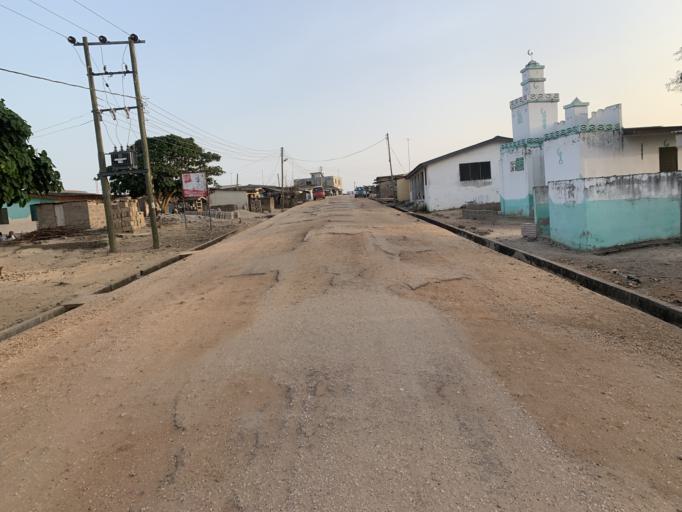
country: GH
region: Central
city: Winneba
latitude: 5.3682
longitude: -0.5843
